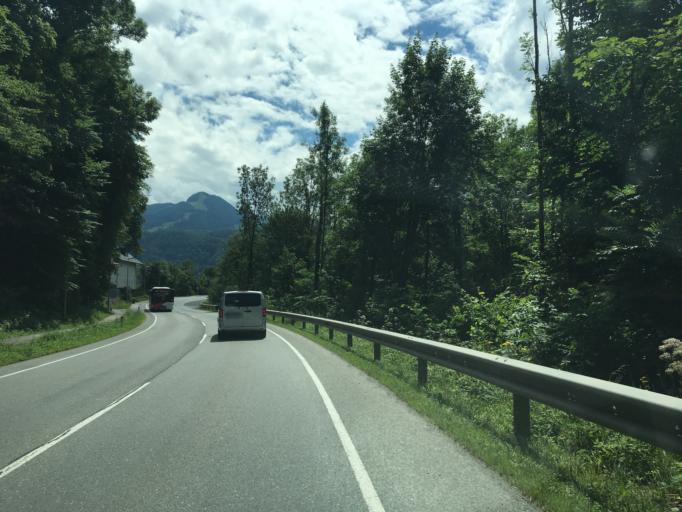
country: AT
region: Salzburg
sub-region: Politischer Bezirk Hallein
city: Oberalm
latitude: 47.6935
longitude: 13.1104
